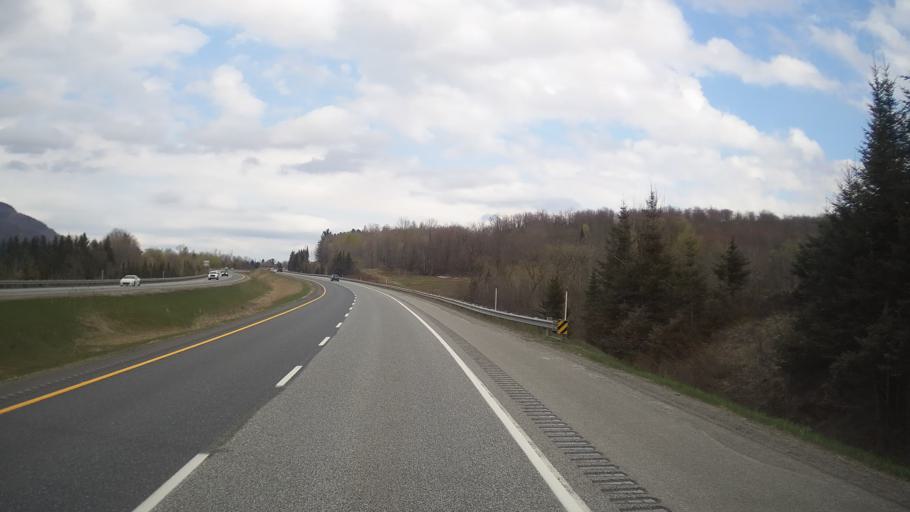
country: CA
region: Quebec
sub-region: Estrie
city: Magog
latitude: 45.2959
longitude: -72.2986
